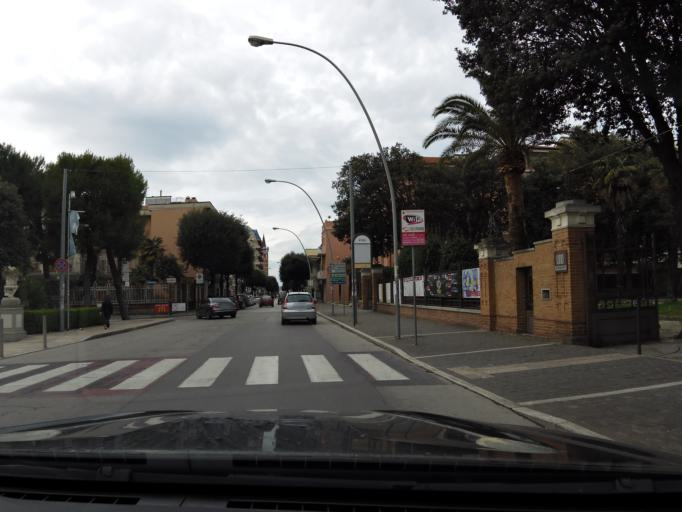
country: IT
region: The Marches
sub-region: Provincia di Macerata
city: Portocivitanova
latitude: 43.3076
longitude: 13.7313
